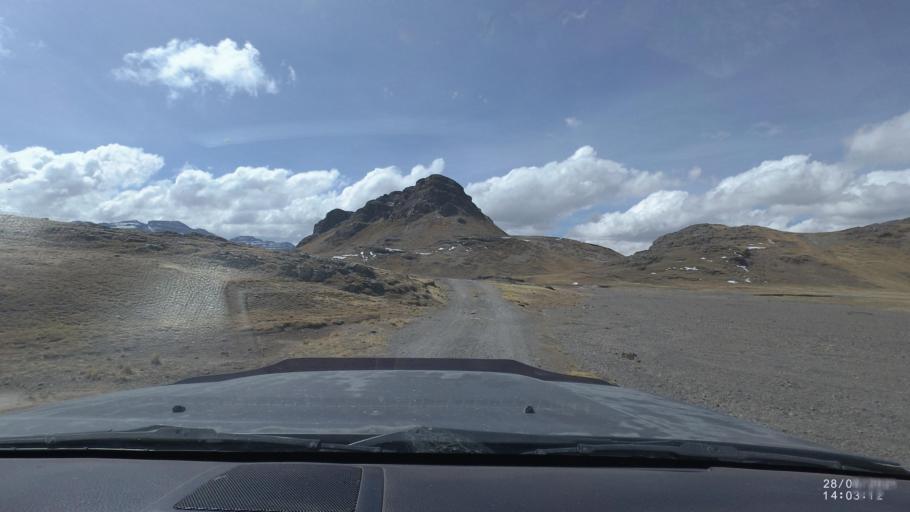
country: BO
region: Cochabamba
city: Sipe Sipe
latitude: -17.2749
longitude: -66.3817
